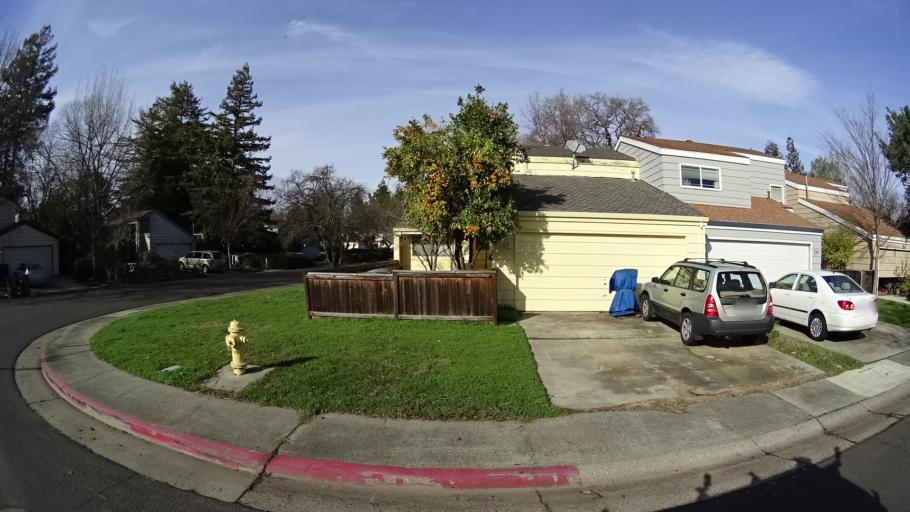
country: US
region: California
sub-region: Yolo County
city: Davis
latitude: 38.5633
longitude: -121.7257
